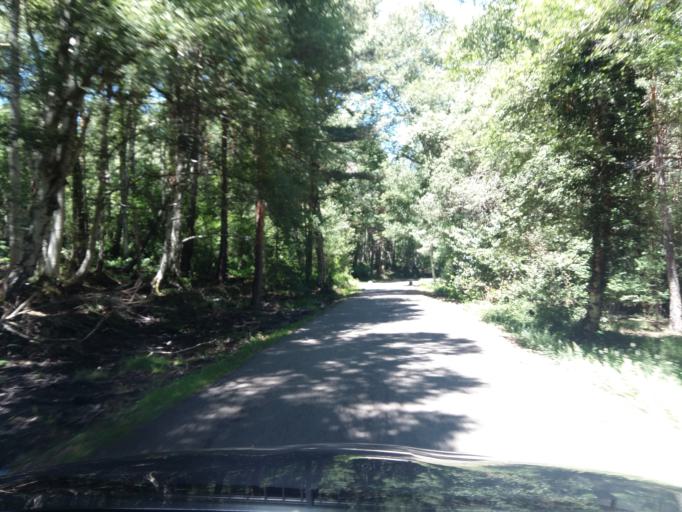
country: ES
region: Castille and Leon
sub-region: Provincia de Soria
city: Vozmediano
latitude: 41.8141
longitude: -1.8242
